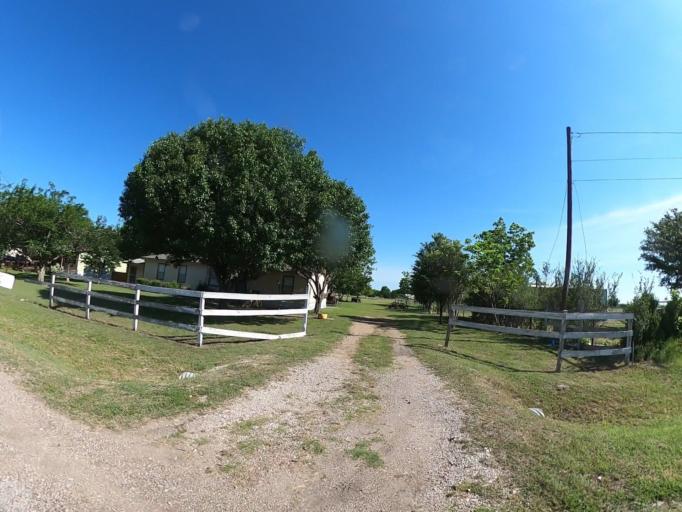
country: US
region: Texas
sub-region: Ellis County
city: Red Oak
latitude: 32.4420
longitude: -96.7791
